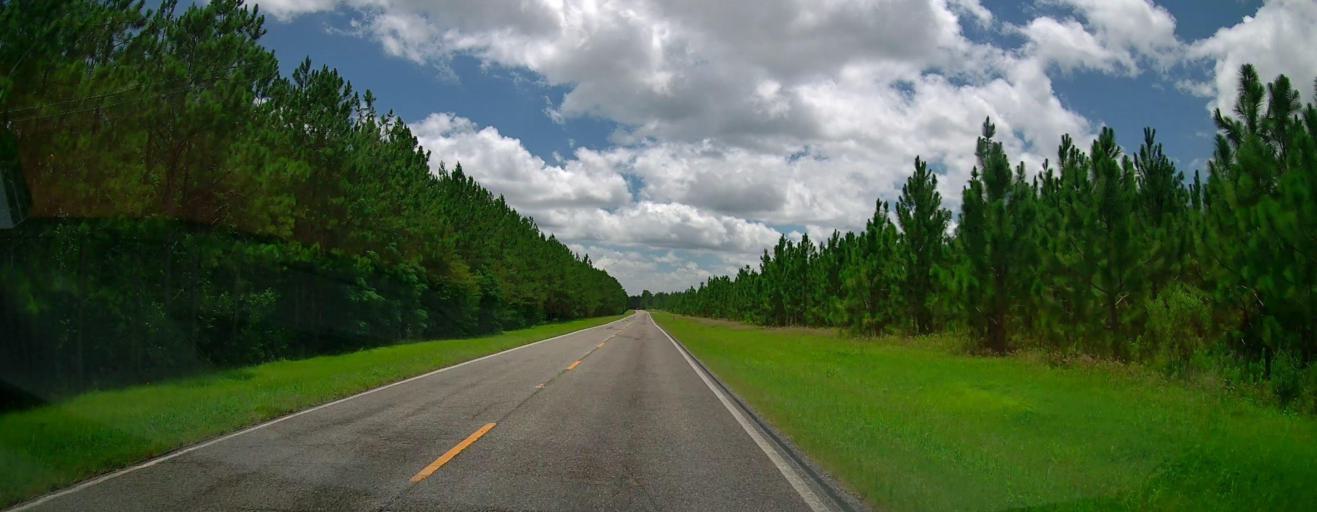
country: US
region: Georgia
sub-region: Wilcox County
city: Rochelle
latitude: 31.8669
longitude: -83.5584
